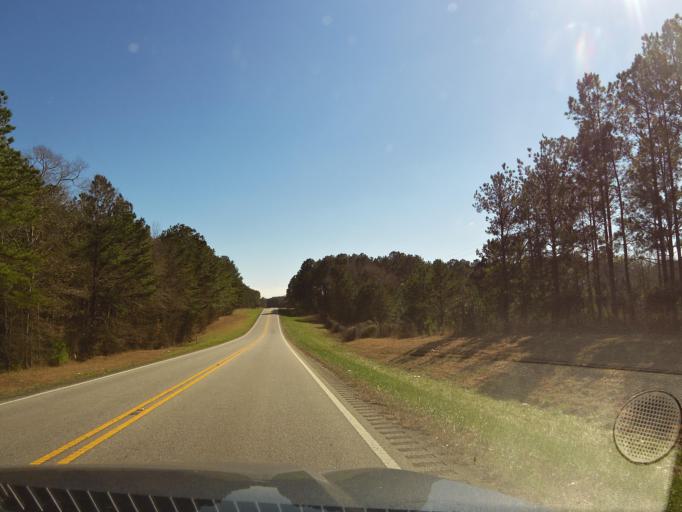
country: US
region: Alabama
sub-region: Bullock County
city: Union Springs
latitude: 32.1189
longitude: -85.5886
